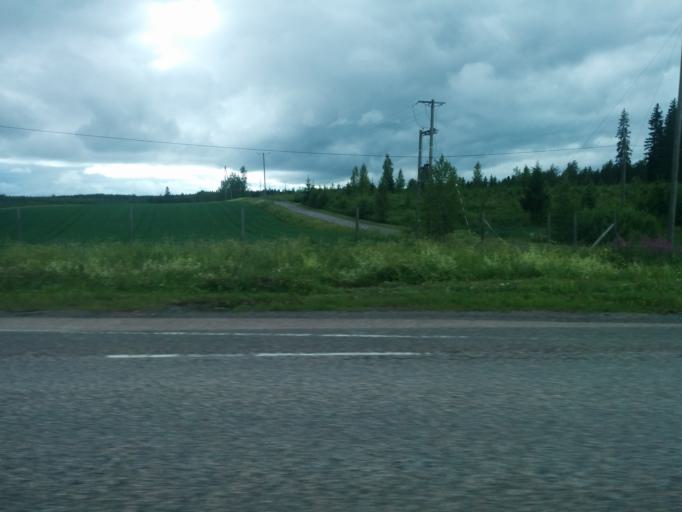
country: FI
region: Pirkanmaa
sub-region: Tampere
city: Orivesi
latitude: 61.7104
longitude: 24.4964
